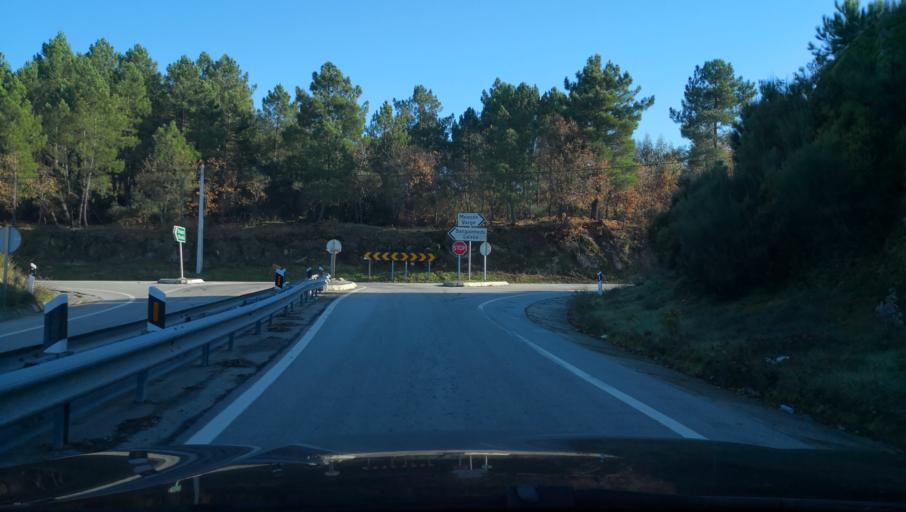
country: PT
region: Vila Real
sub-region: Vila Real
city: Vila Real
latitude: 41.3280
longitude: -7.6743
